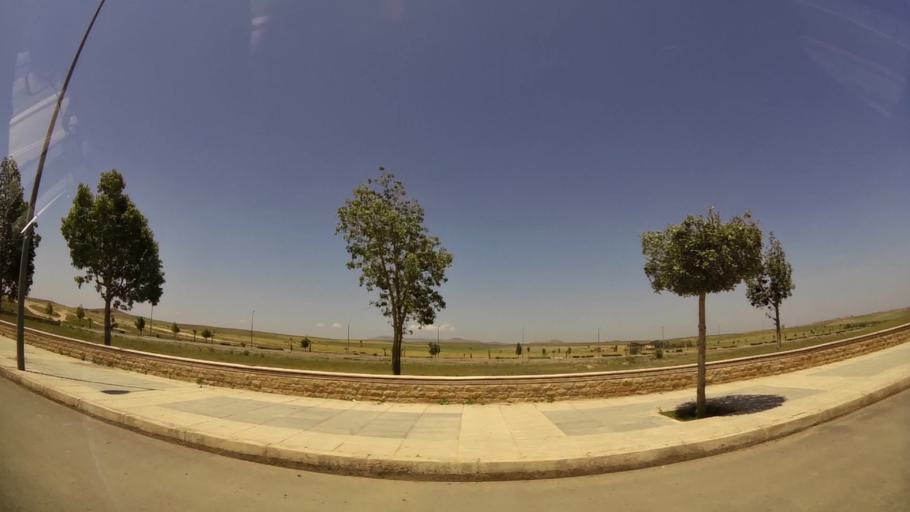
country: MA
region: Oriental
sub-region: Oujda-Angad
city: Oujda
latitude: 34.6562
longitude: -1.9559
